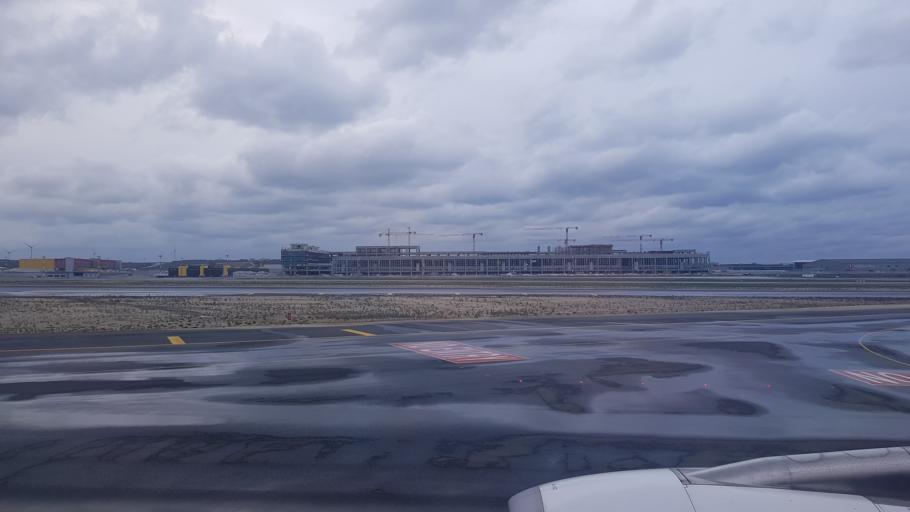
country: TR
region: Istanbul
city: Durusu
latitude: 41.2768
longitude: 28.7296
